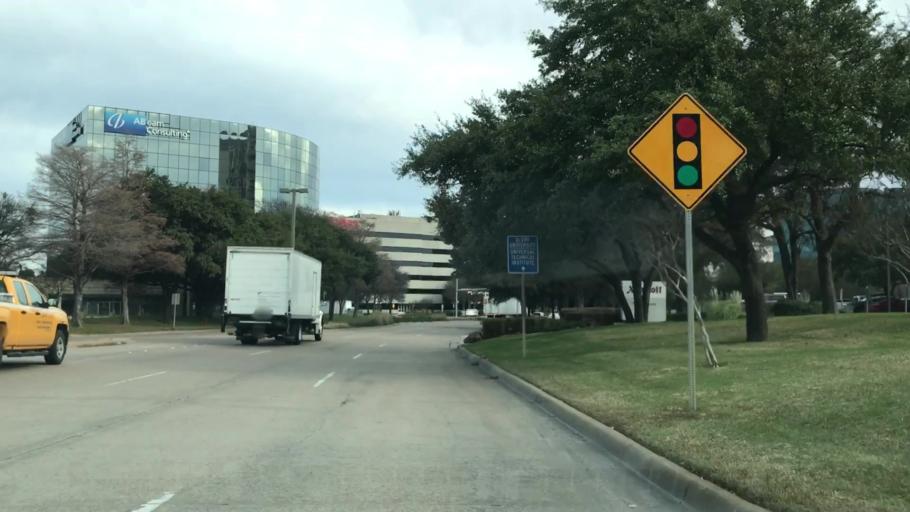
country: US
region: Texas
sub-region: Dallas County
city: Coppell
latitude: 32.9222
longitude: -97.0198
